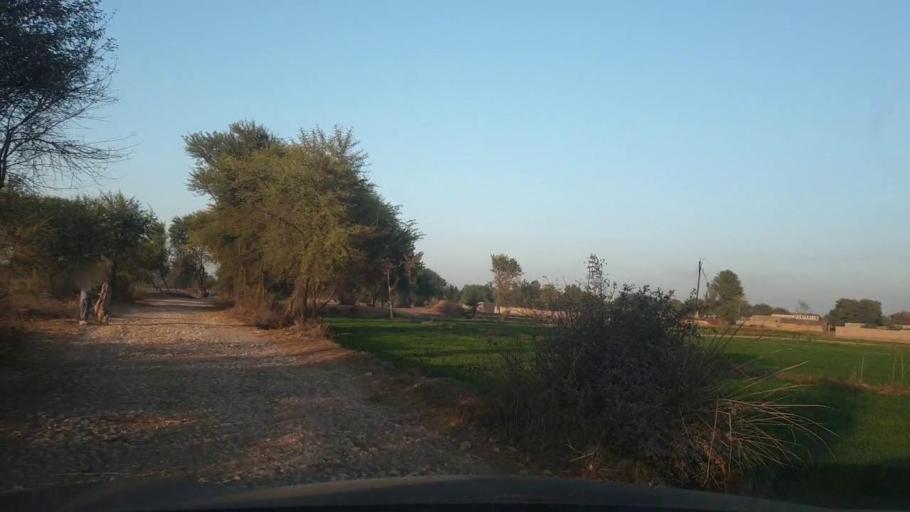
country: PK
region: Sindh
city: Ubauro
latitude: 28.1769
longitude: 69.6035
